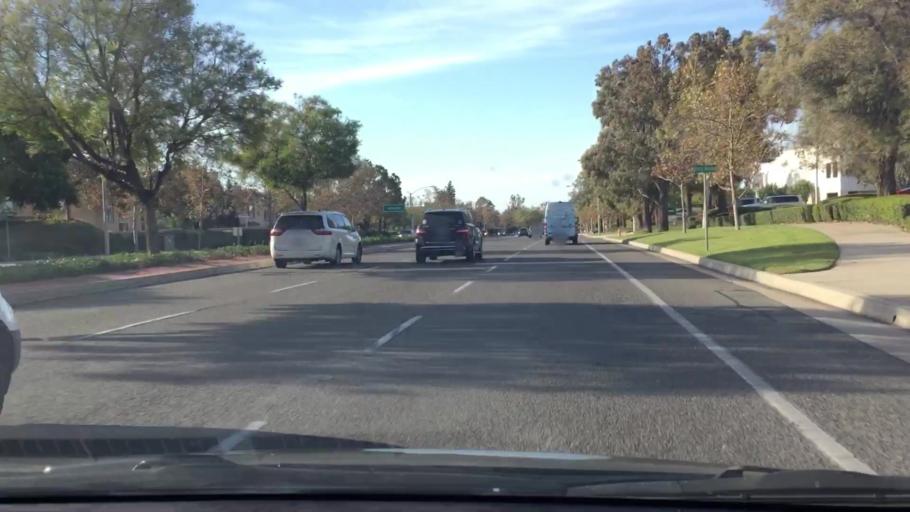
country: US
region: California
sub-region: Orange County
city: Rancho Santa Margarita
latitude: 33.6244
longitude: -117.6079
